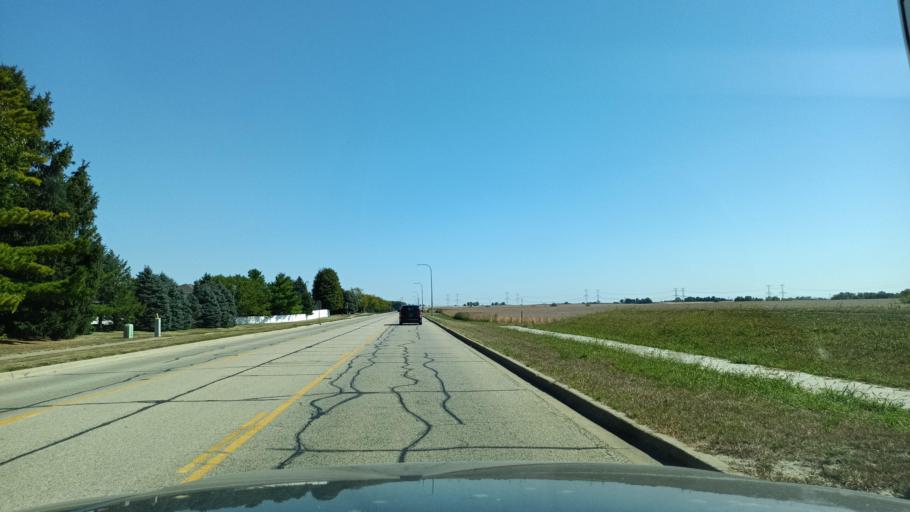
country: US
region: Illinois
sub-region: Tazewell County
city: Morton
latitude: 40.6132
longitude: -89.4391
